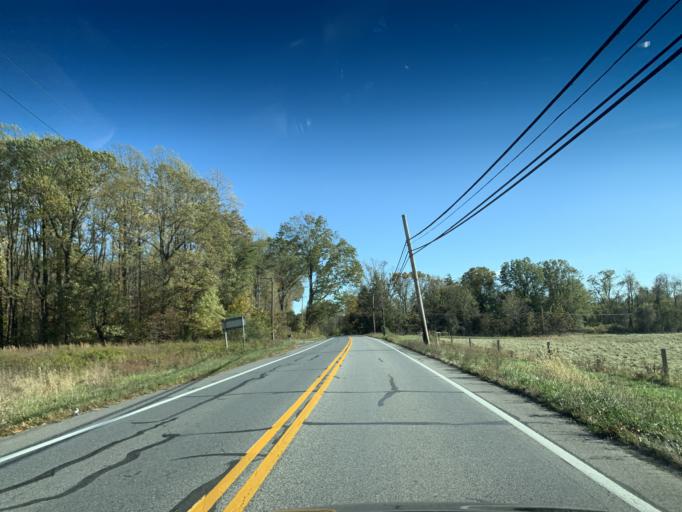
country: US
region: Maryland
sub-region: Anne Arundel County
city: Gambrills
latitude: 39.0591
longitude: -76.6612
